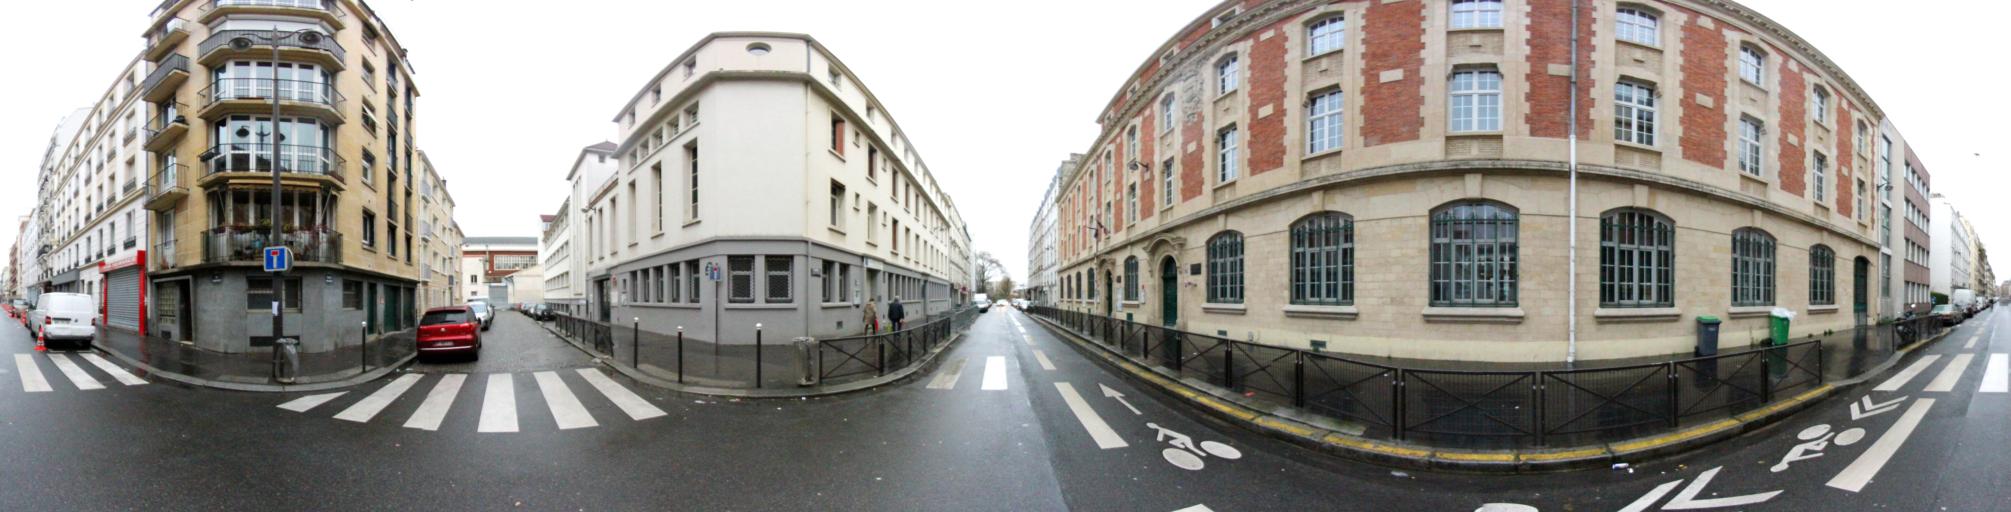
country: FR
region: Ile-de-France
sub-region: Paris
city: Saint-Ouen
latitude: 48.8953
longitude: 2.3516
